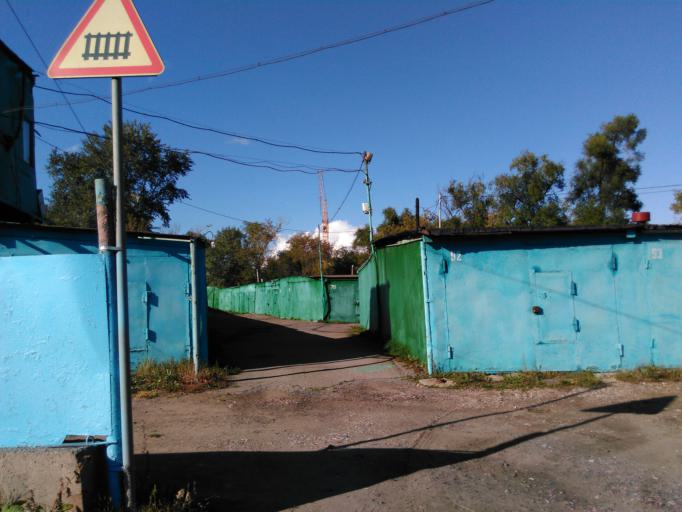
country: RU
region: Moscow
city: Likhobory
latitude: 55.8487
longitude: 37.5746
